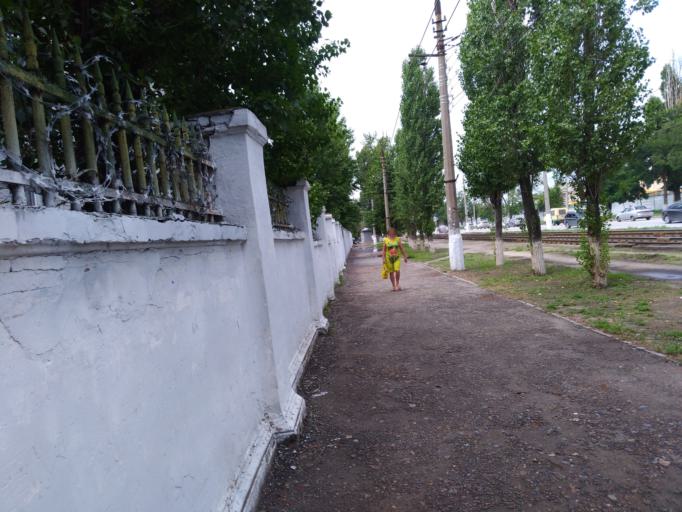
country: RU
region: Volgograd
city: Volgograd
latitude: 48.7166
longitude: 44.4853
